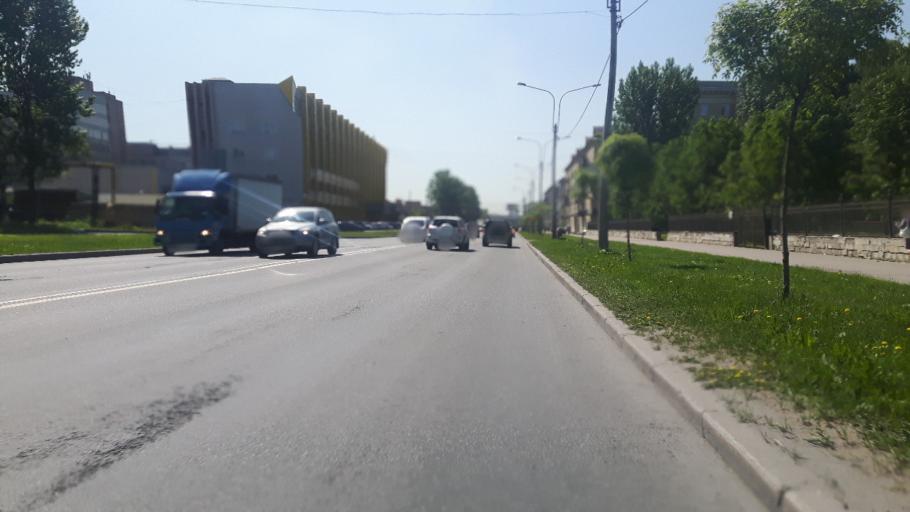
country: RU
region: St.-Petersburg
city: Admiralteisky
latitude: 59.8909
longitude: 30.2792
